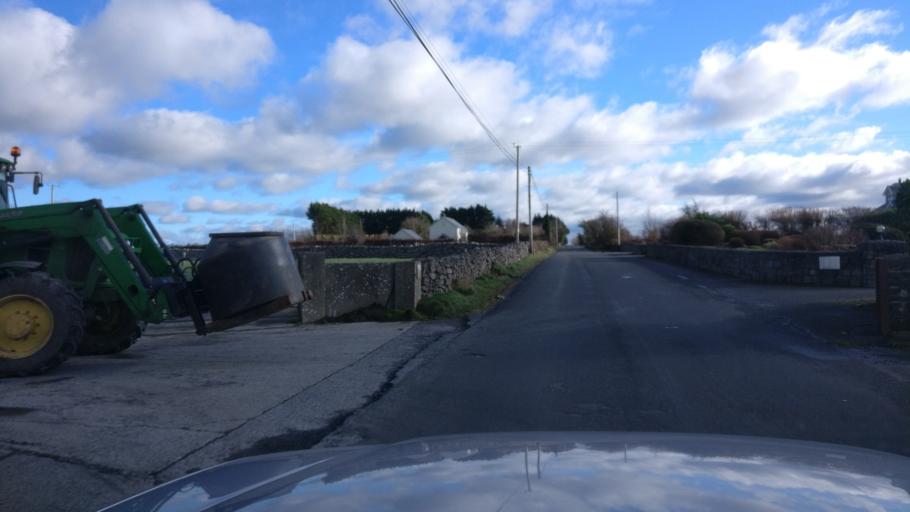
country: IE
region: Connaught
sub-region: County Galway
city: Oranmore
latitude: 53.2640
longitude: -8.8676
